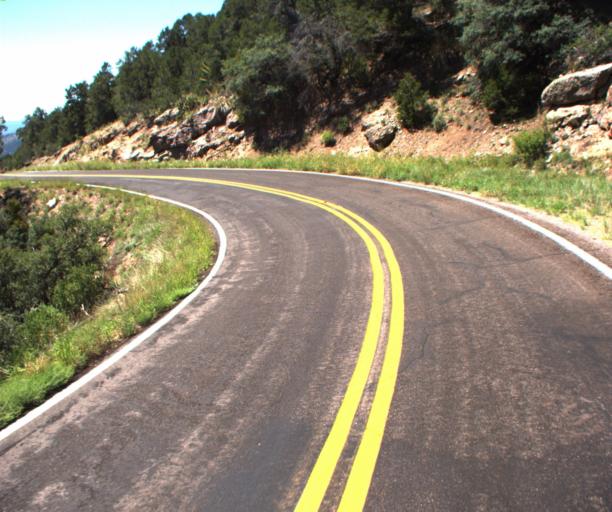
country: US
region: Arizona
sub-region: Greenlee County
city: Morenci
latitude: 33.3920
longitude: -109.3313
